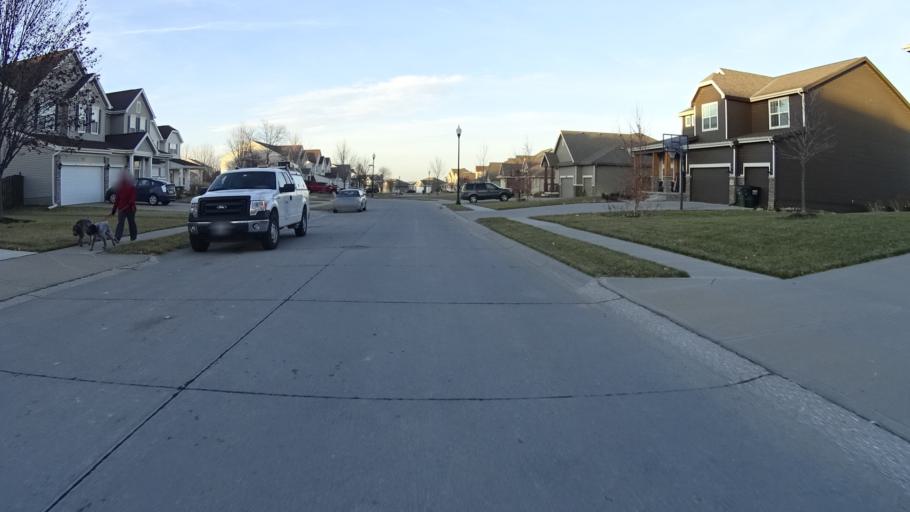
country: US
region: Nebraska
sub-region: Sarpy County
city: Papillion
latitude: 41.1290
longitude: -96.0686
